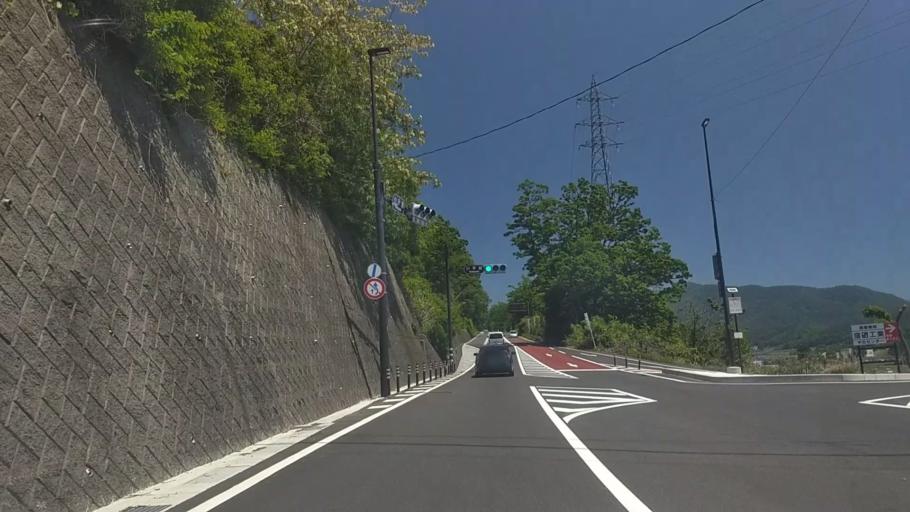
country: JP
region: Yamanashi
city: Nirasaki
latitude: 35.8012
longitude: 138.4253
